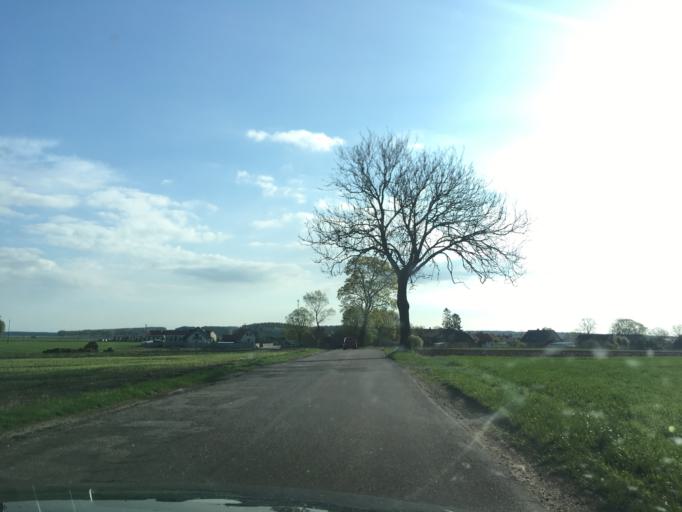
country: PL
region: Warmian-Masurian Voivodeship
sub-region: Powiat nidzicki
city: Kozlowo
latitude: 53.4075
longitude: 20.3246
